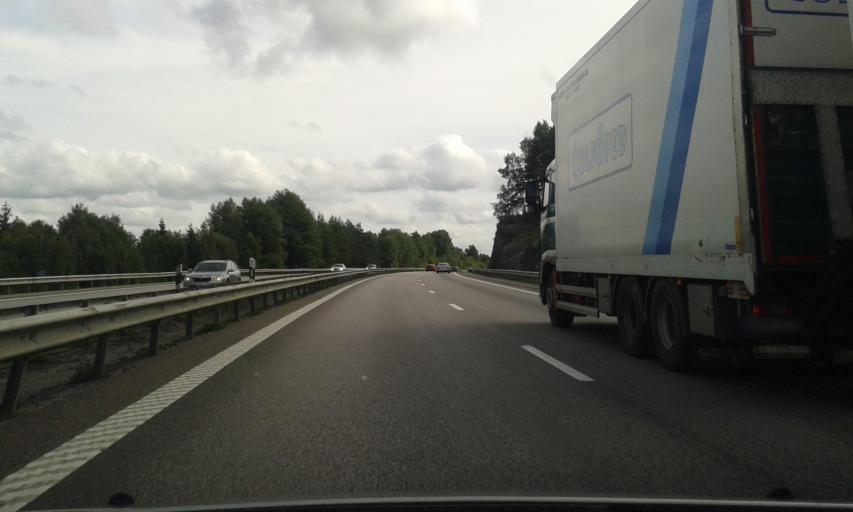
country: SE
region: Halland
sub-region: Kungsbacka Kommun
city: Fjaeras kyrkby
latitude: 57.3979
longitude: 12.1878
